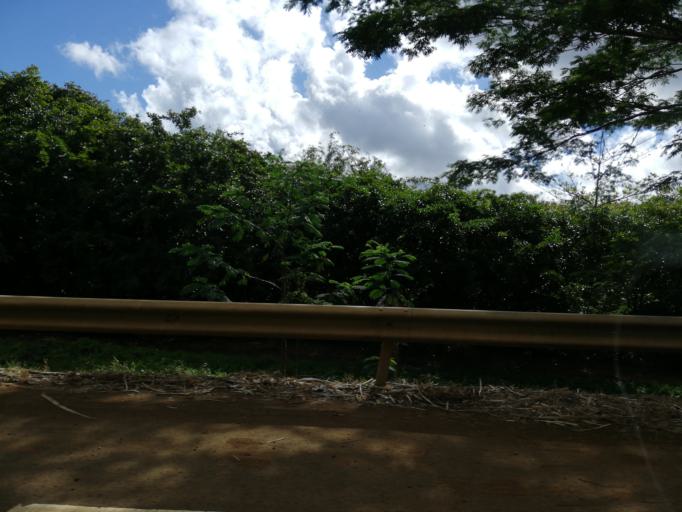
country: MU
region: Grand Port
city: Bois des Amourettes
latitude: -20.3709
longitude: 57.7010
